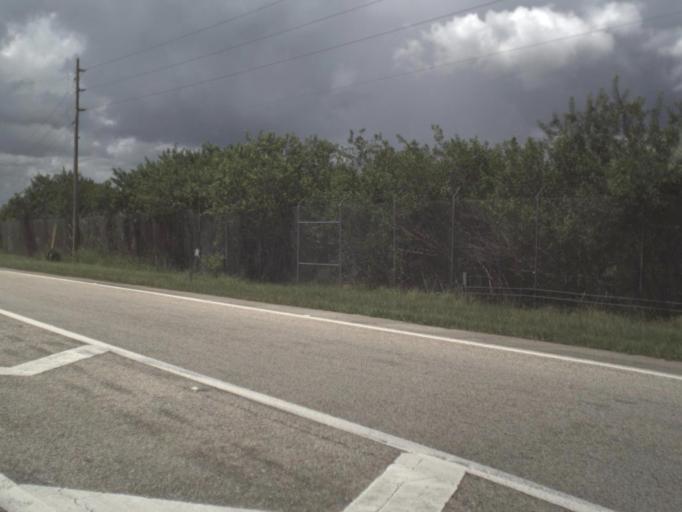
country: US
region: Florida
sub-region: Collier County
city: Immokalee
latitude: 26.1549
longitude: -81.3403
